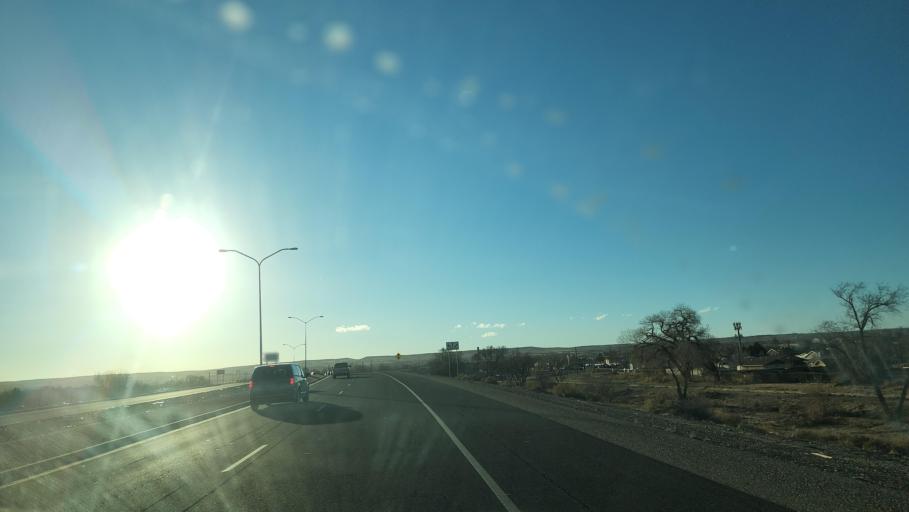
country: US
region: New Mexico
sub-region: Bernalillo County
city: South Valley
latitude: 35.0278
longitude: -106.7103
